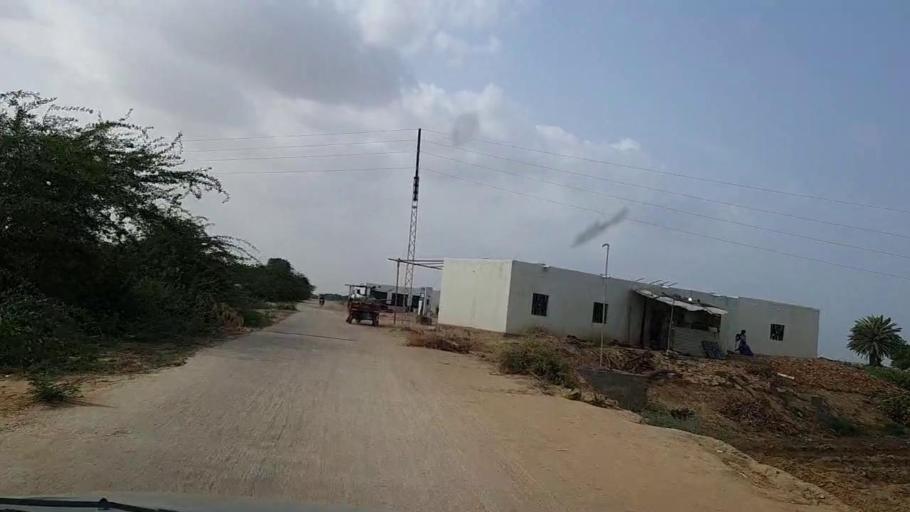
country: PK
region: Sindh
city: Kotri
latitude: 25.2558
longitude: 68.2568
